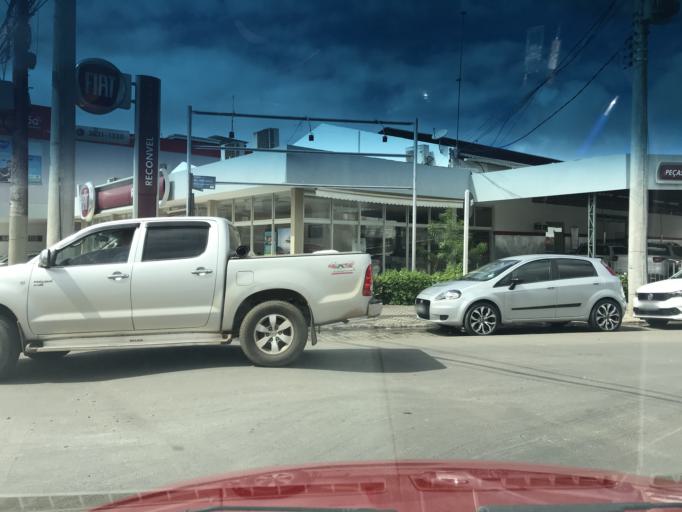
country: BR
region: Bahia
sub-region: Santo Antonio De Jesus
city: Santo Antonio de Jesus
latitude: -12.9663
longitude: -39.2696
